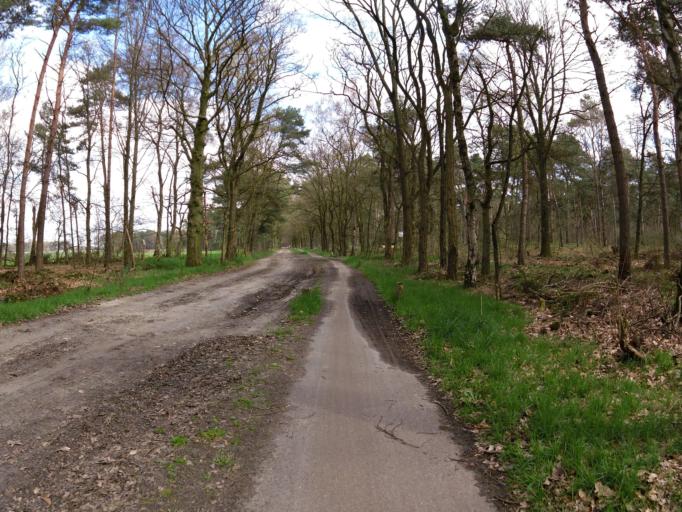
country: NL
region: North Brabant
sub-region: Gemeente Haaren
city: Haaren
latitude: 51.5556
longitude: 5.2478
